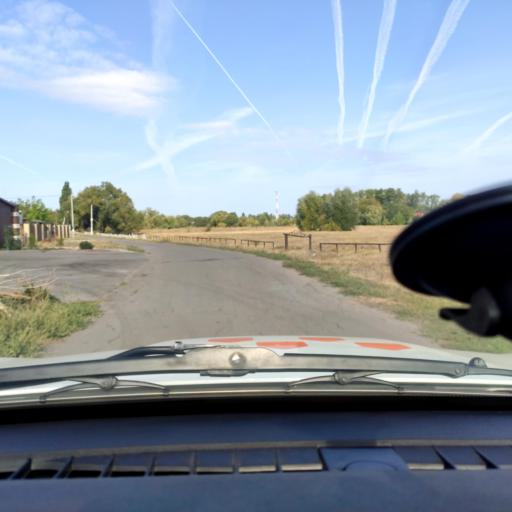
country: RU
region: Voronezj
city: Novaya Usman'
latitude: 51.6290
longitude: 39.4111
